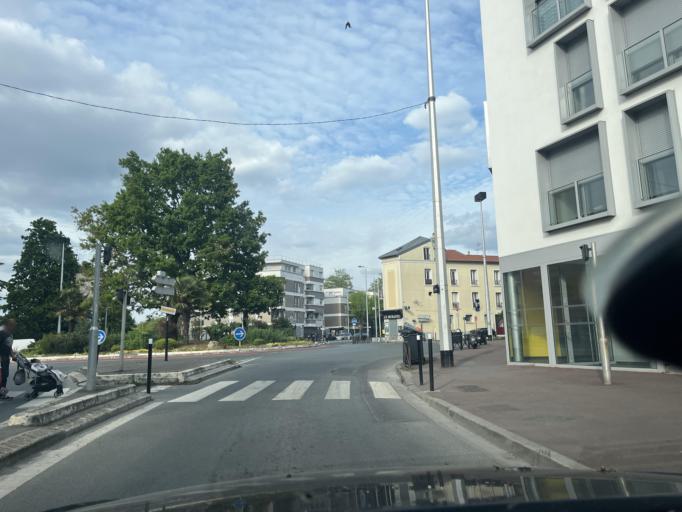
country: FR
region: Ile-de-France
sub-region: Departement de Seine-Saint-Denis
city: La Courneuve
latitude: 48.9317
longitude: 2.3986
